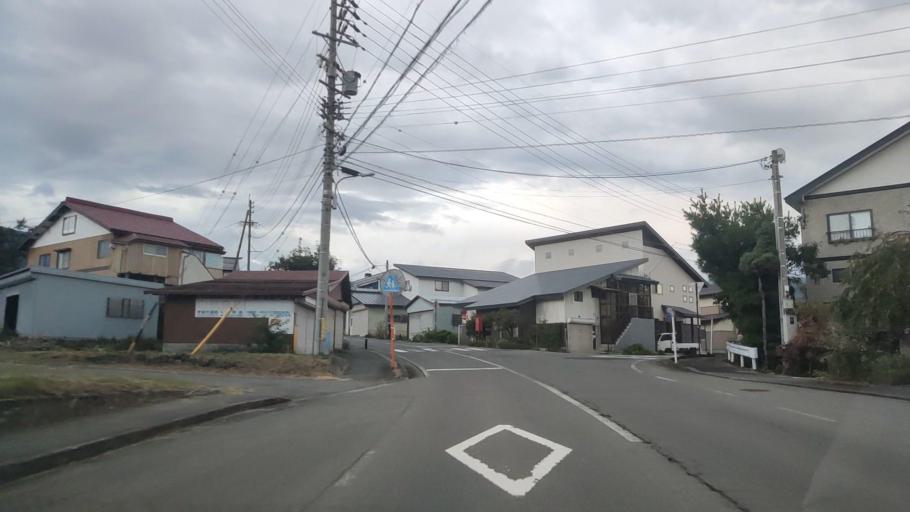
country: JP
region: Nagano
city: Iiyama
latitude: 36.8550
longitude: 138.4089
